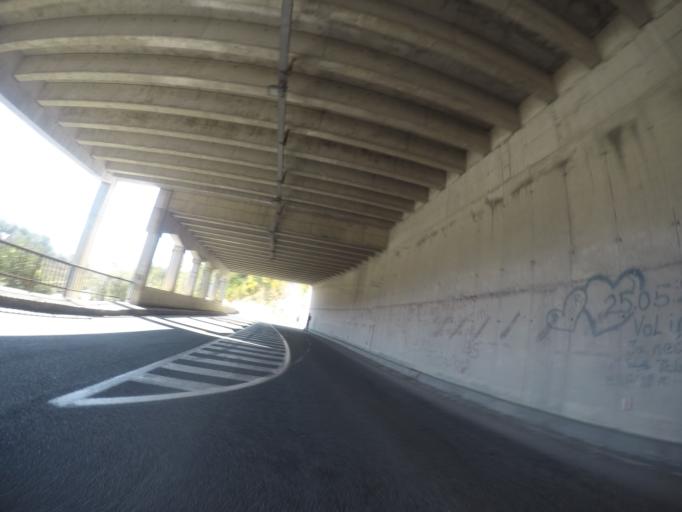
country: ME
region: Opstina Kolasin
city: Kolasin
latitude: 42.8288
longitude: 19.5137
